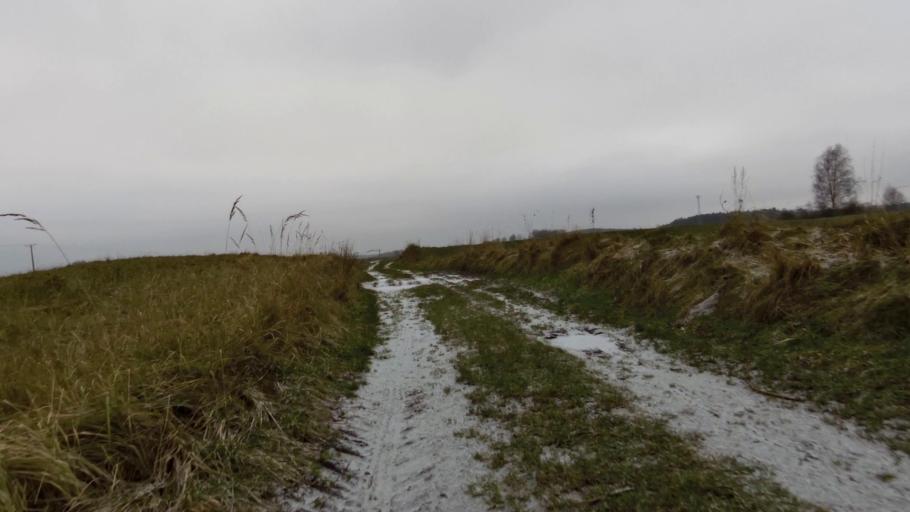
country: PL
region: West Pomeranian Voivodeship
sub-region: Powiat szczecinecki
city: Szczecinek
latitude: 53.6451
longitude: 16.6189
